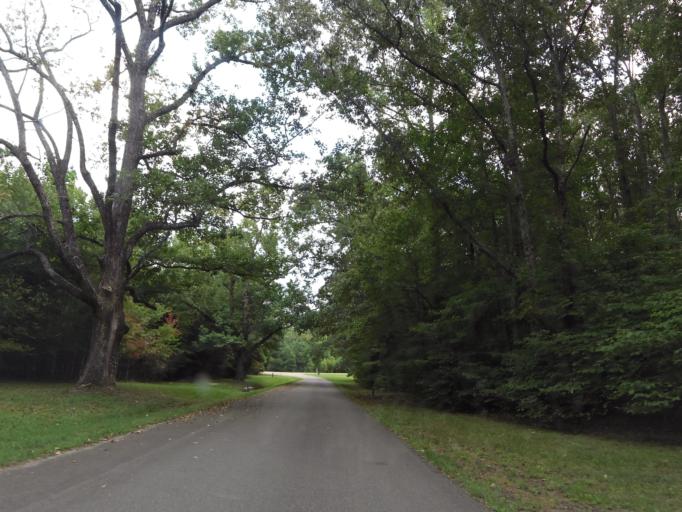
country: US
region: Tennessee
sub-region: Hardin County
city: Crump
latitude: 35.1245
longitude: -88.3432
